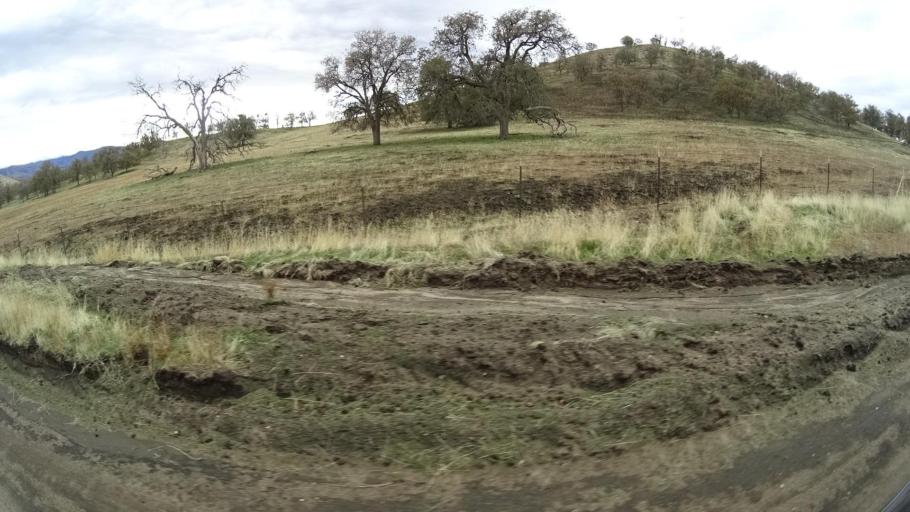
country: US
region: California
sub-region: Kern County
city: Stallion Springs
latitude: 35.1215
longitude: -118.7052
